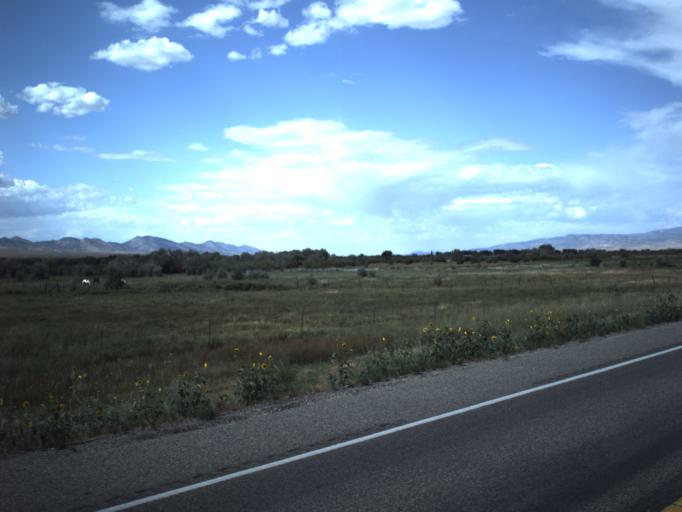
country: US
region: Utah
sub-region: Sevier County
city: Salina
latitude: 38.9863
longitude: -111.8502
